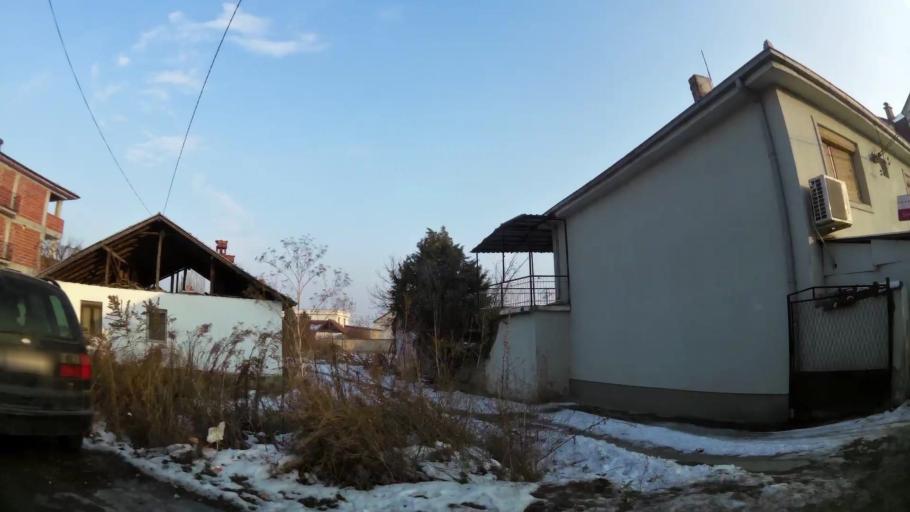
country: MK
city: Creshevo
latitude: 42.0175
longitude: 21.5131
